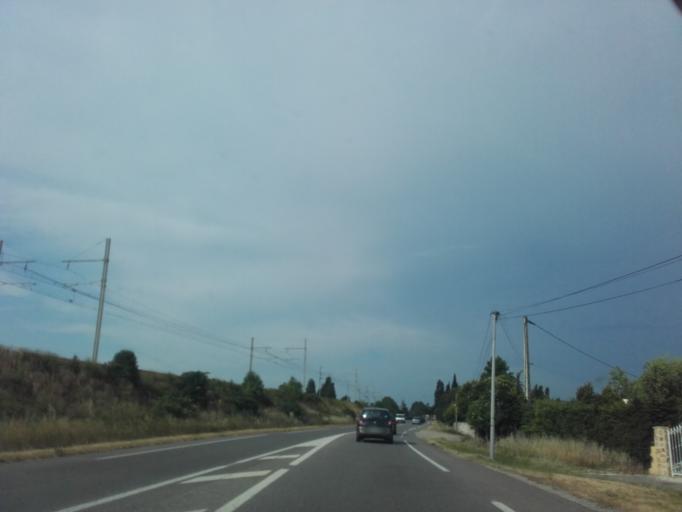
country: FR
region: Rhone-Alpes
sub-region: Departement de la Drome
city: Loriol-sur-Drome
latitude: 44.7486
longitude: 4.8103
